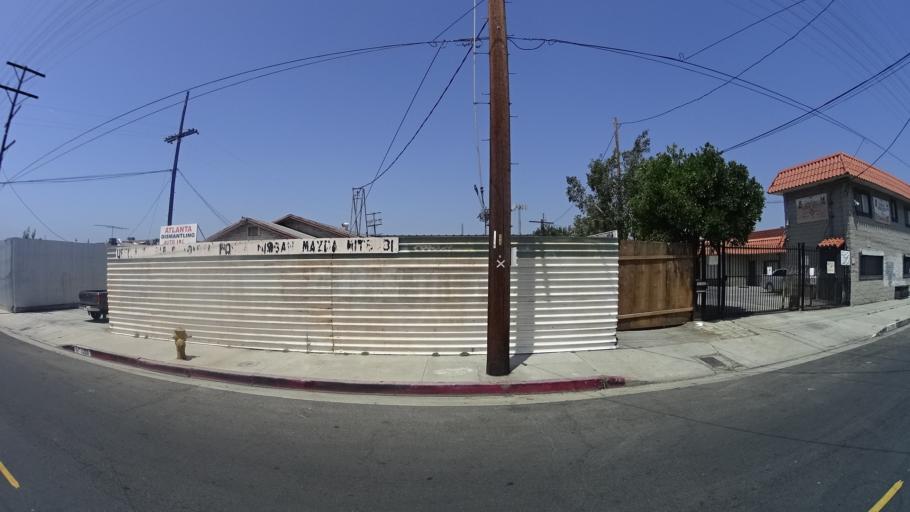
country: US
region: California
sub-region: Los Angeles County
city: Van Nuys
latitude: 34.2028
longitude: -118.4225
